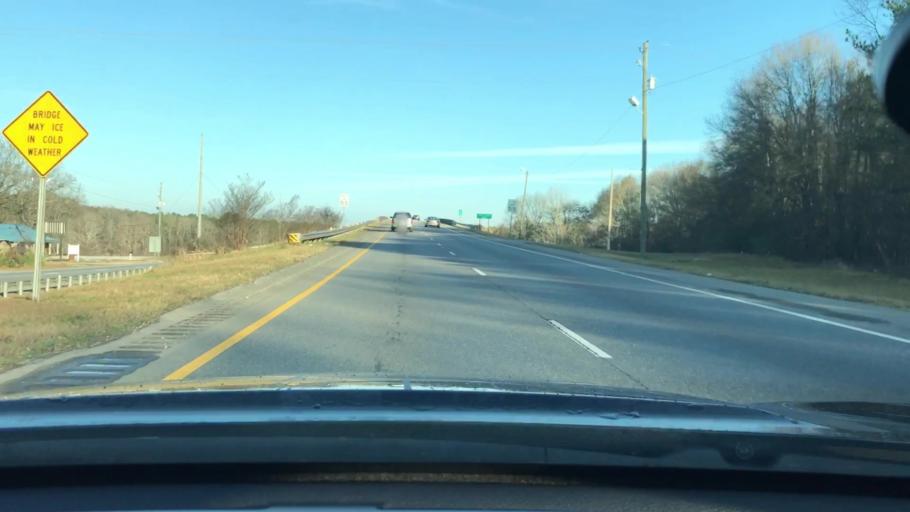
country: US
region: Alabama
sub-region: Talladega County
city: Childersburg
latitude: 33.2880
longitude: -86.3637
